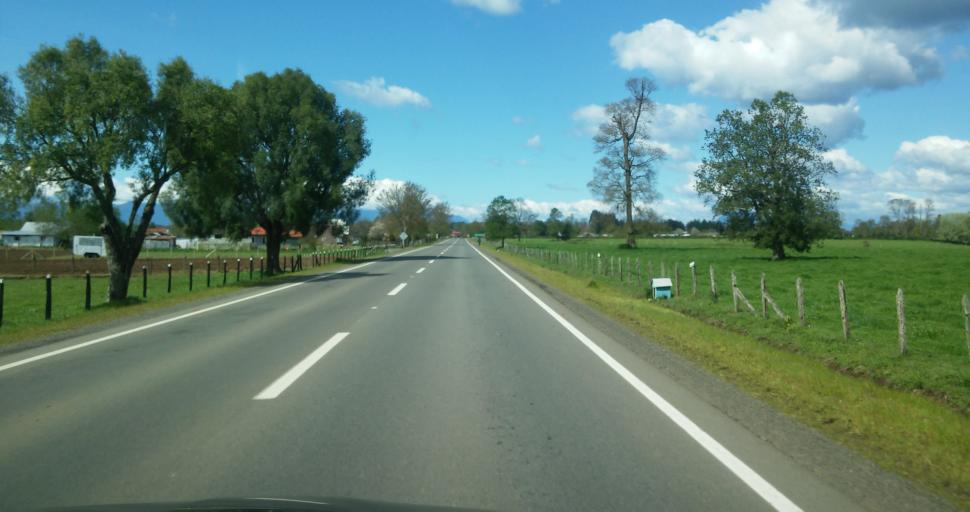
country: CL
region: Los Rios
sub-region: Provincia del Ranco
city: Rio Bueno
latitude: -40.2402
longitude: -72.6027
